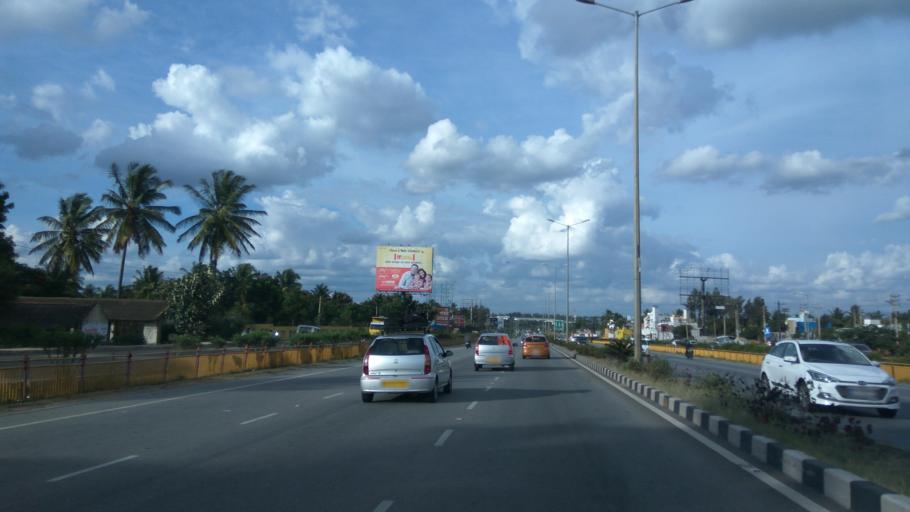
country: IN
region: Karnataka
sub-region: Bangalore Urban
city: Yelahanka
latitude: 13.1680
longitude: 77.6312
